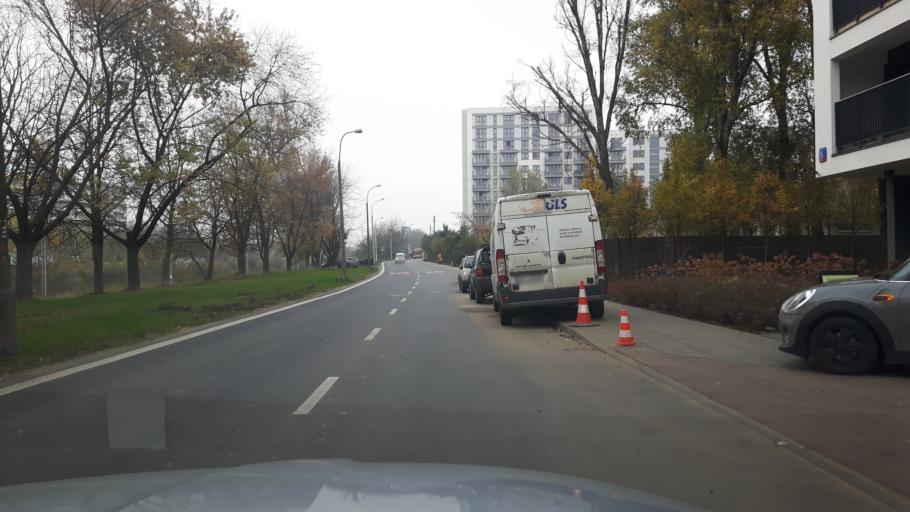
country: PL
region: Masovian Voivodeship
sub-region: Warszawa
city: Wlochy
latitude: 52.1979
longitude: 20.9599
